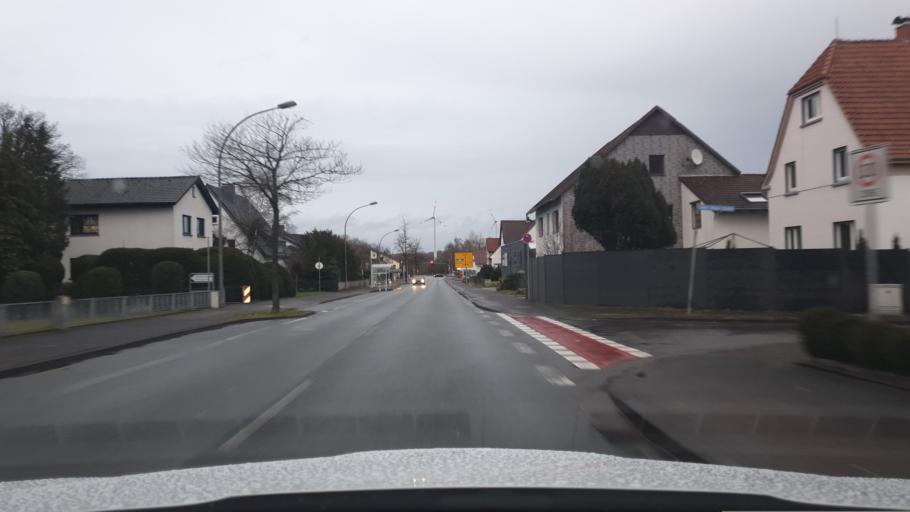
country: DE
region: North Rhine-Westphalia
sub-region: Regierungsbezirk Detmold
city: Lage
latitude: 51.9528
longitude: 8.8120
